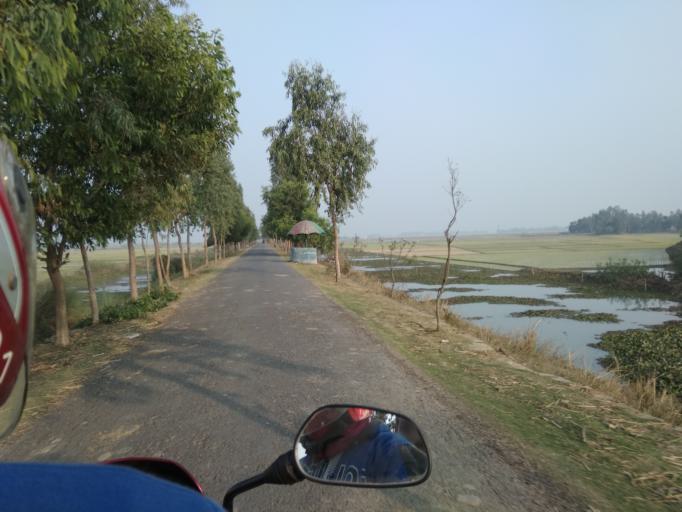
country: BD
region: Rajshahi
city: Par Naogaon
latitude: 24.4987
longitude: 89.1705
